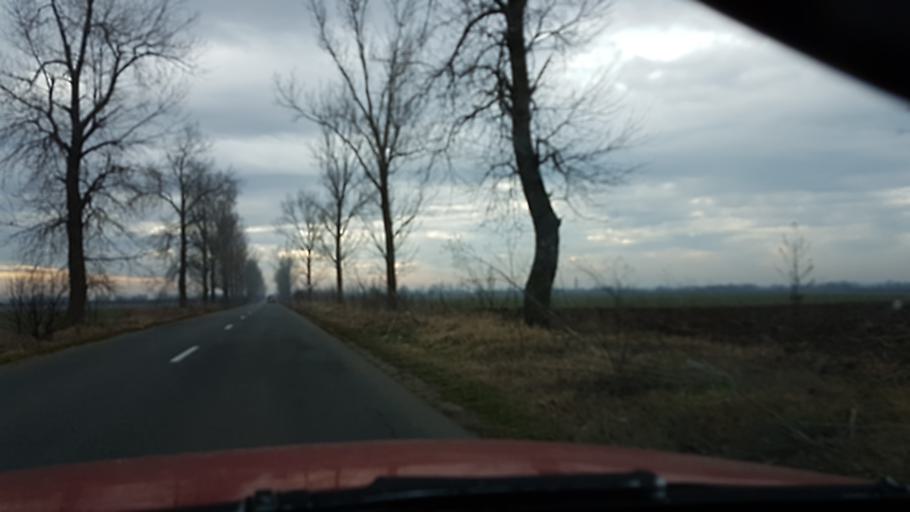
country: RO
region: Giurgiu
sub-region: Comuna Herasti
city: Herasti
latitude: 44.2277
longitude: 26.3608
